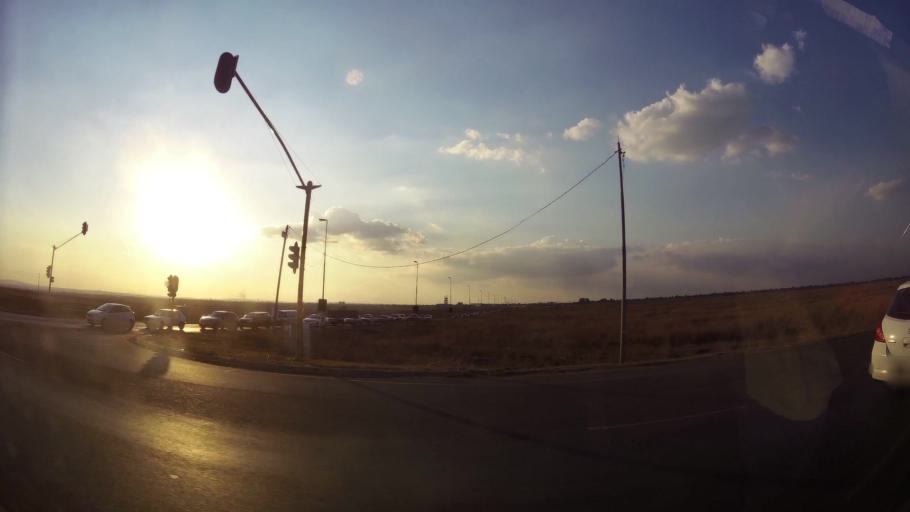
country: ZA
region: Gauteng
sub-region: Ekurhuleni Metropolitan Municipality
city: Boksburg
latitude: -26.2748
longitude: 28.2739
